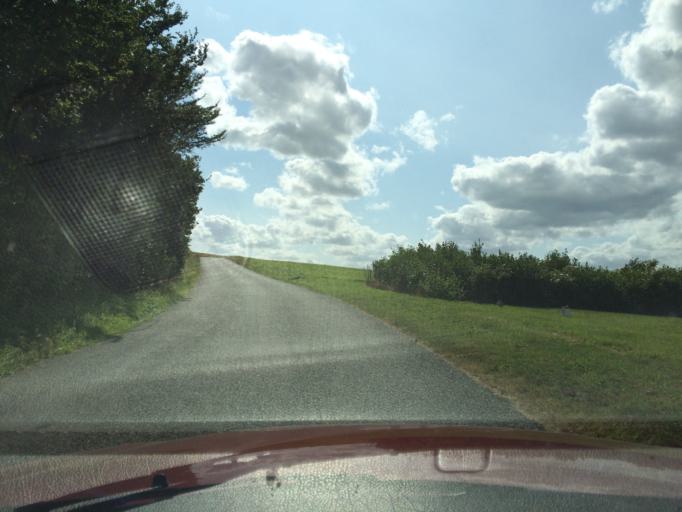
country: DK
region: Central Jutland
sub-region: Skanderborg Kommune
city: Galten
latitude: 56.1592
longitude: 9.8816
